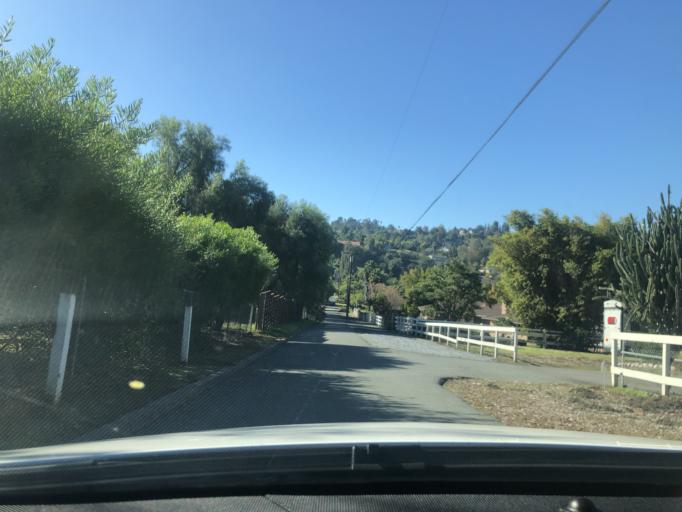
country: US
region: California
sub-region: San Diego County
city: El Cajon
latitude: 32.7792
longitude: -116.9416
